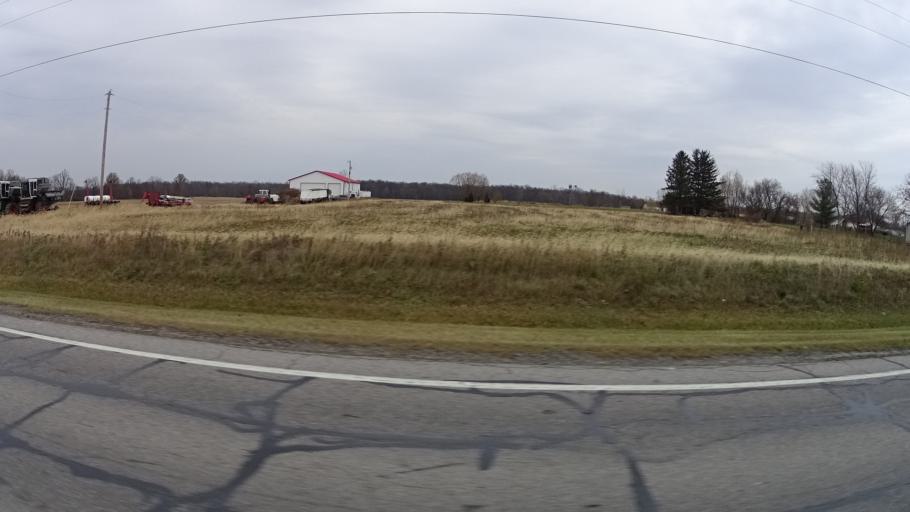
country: US
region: Ohio
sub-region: Lorain County
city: Lagrange
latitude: 41.1683
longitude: -82.0865
